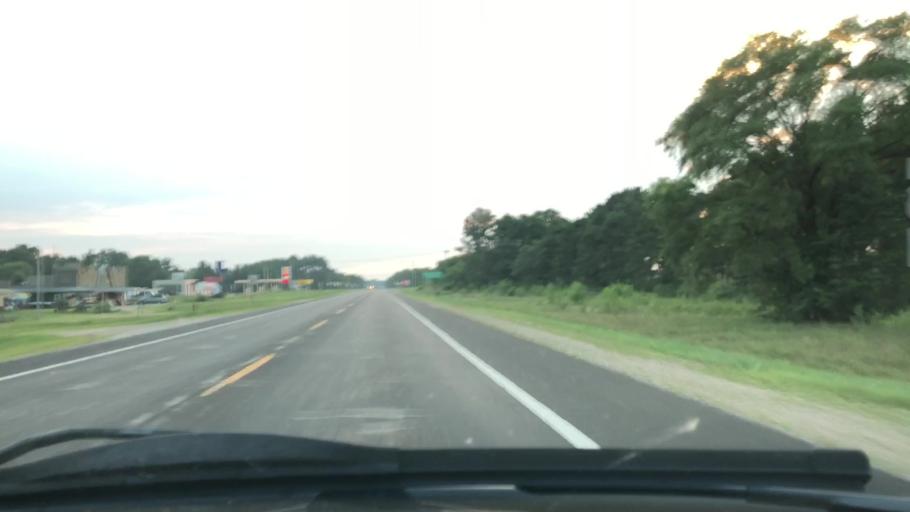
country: US
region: Wisconsin
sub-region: Sauk County
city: Spring Green
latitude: 43.1913
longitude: -90.1950
